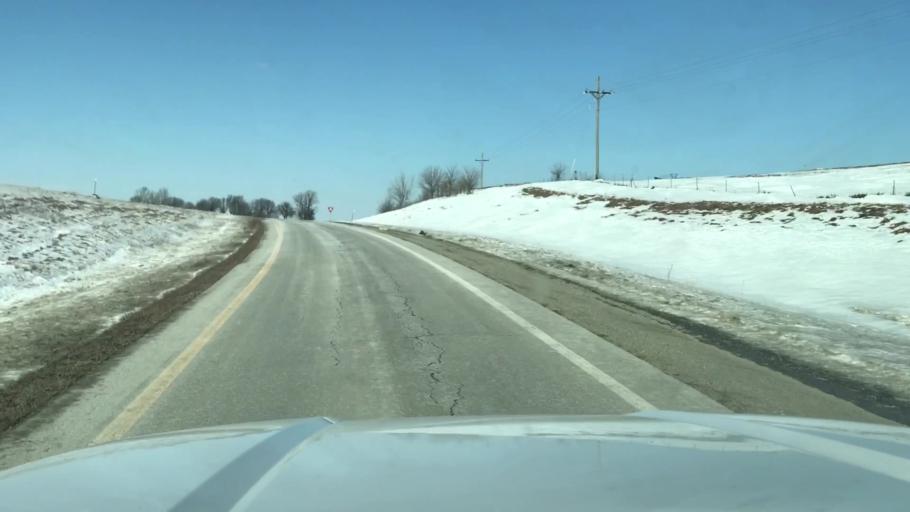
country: US
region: Missouri
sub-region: Andrew County
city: Savannah
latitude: 39.9631
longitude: -94.8620
